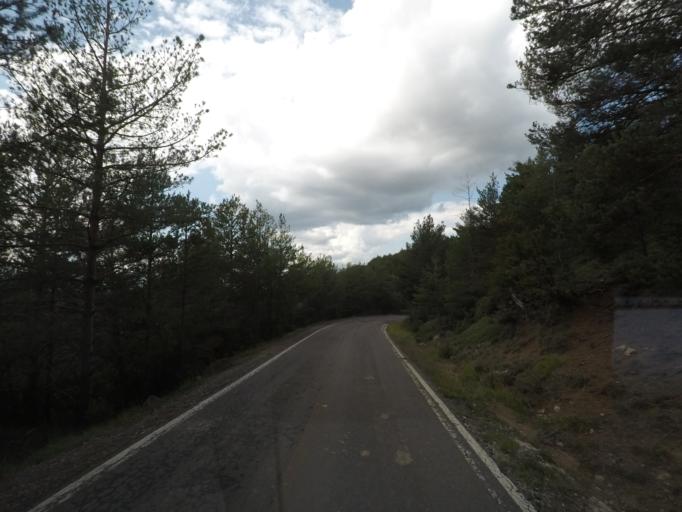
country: ES
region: Aragon
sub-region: Provincia de Huesca
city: Fiscal
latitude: 42.4086
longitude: -0.0975
